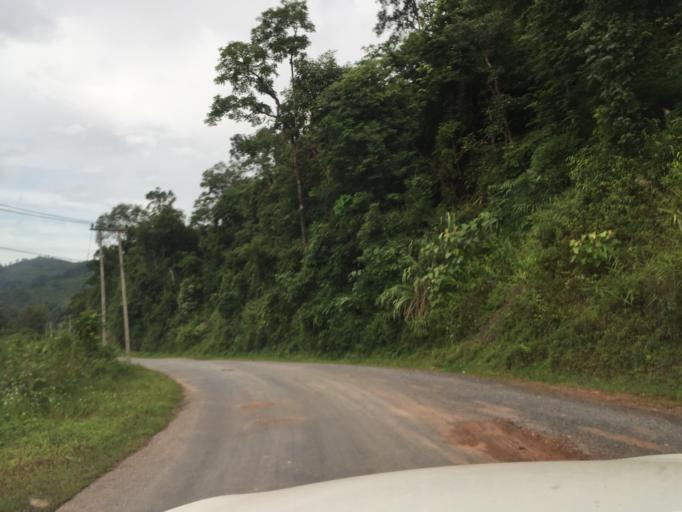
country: LA
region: Phongsali
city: Phongsali
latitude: 21.3392
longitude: 102.0477
